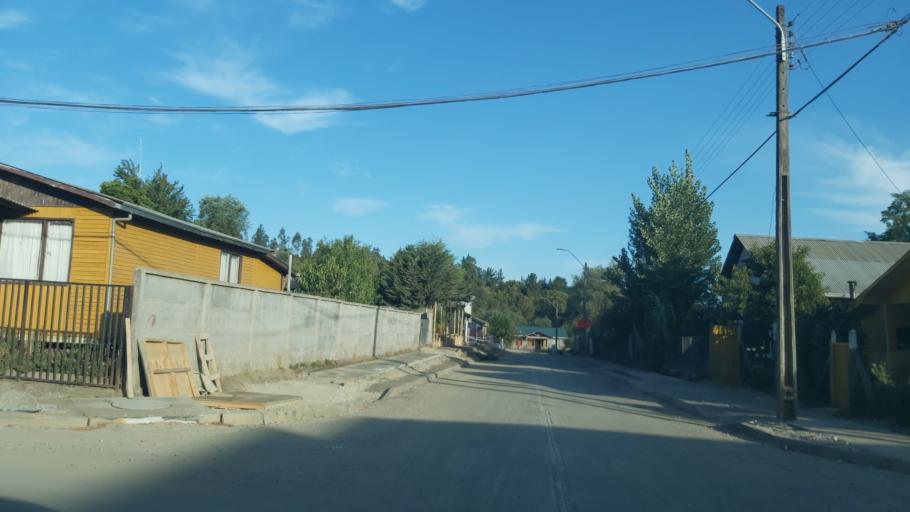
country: CL
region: Biobio
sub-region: Provincia de Biobio
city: La Laja
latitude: -37.1632
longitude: -72.9074
